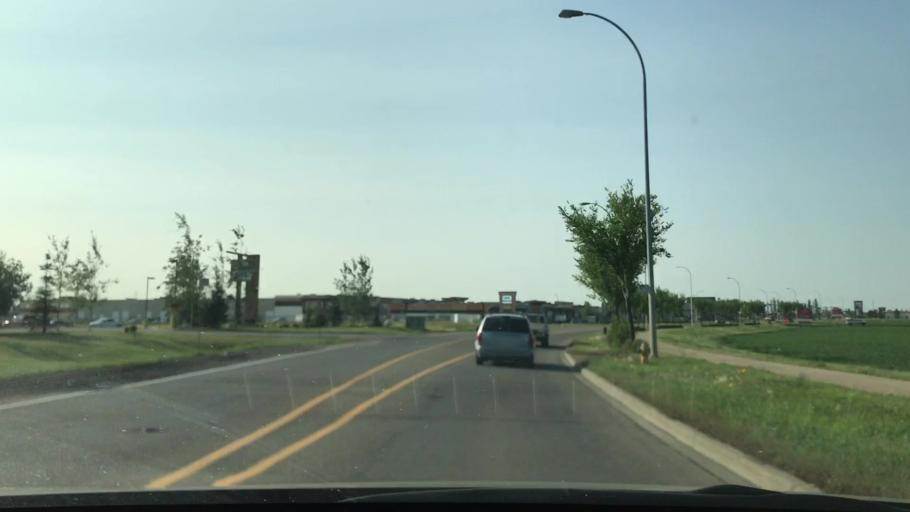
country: CA
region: Alberta
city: Beaumont
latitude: 53.4322
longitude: -113.4807
